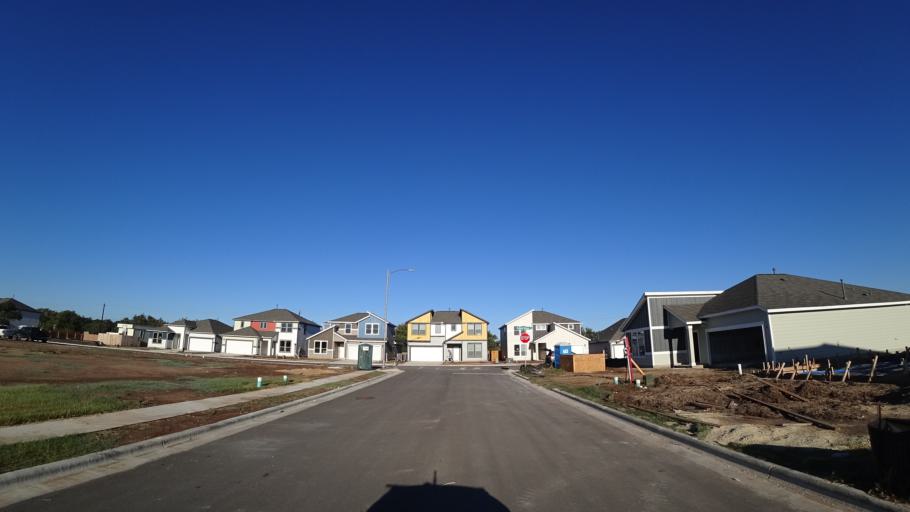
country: US
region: Texas
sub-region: Travis County
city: Hornsby Bend
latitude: 30.2205
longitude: -97.6338
